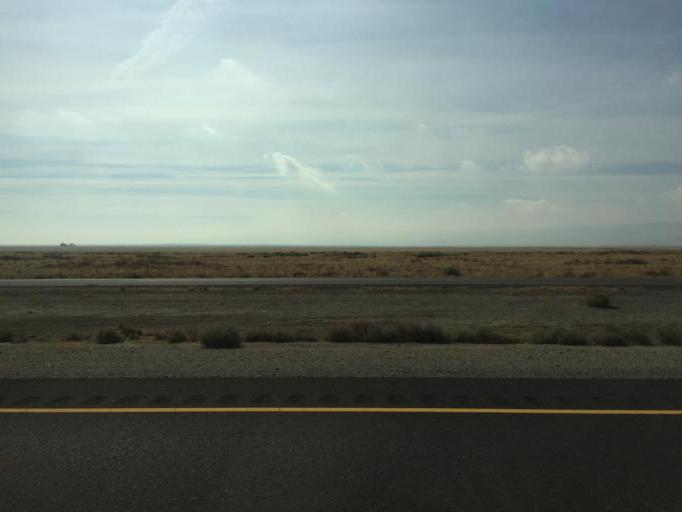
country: US
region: California
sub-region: Kern County
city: Lost Hills
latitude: 35.6149
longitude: -119.8806
